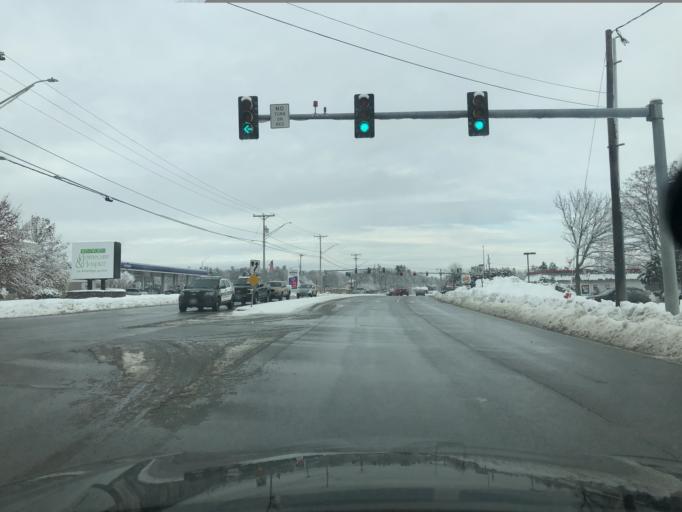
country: US
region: New Hampshire
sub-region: Strafford County
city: Somersworth
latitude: 43.2345
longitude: -70.8816
